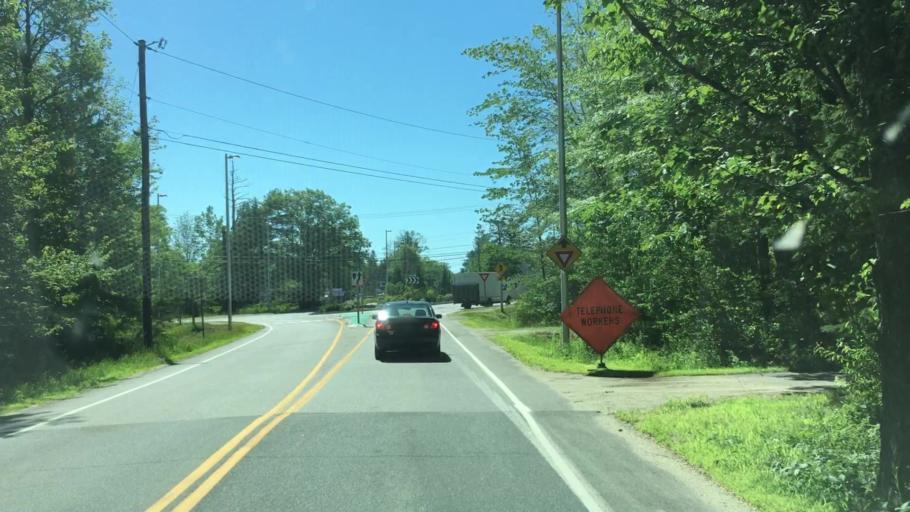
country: US
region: Maine
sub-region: Hancock County
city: Sedgwick
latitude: 44.4087
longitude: -68.5984
